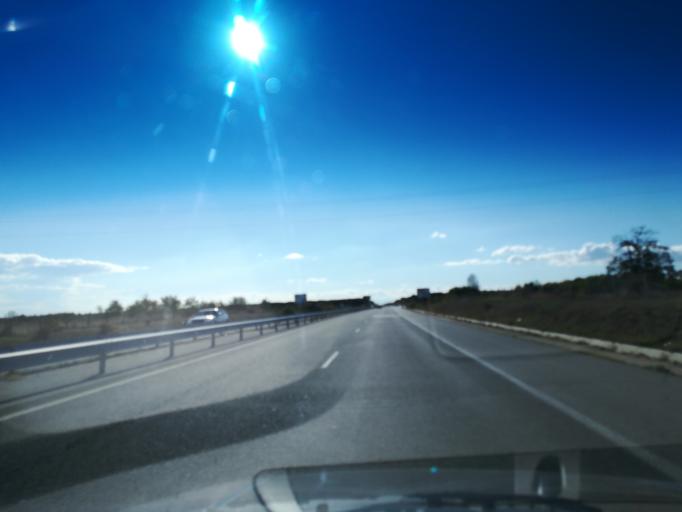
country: BG
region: Stara Zagora
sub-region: Obshtina Nikolaevo
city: Elkhovo
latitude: 42.2796
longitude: 25.4546
